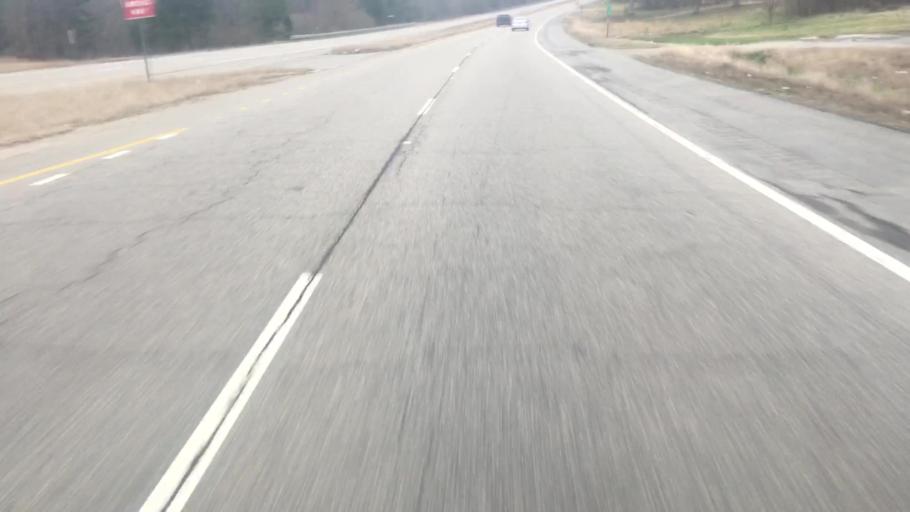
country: US
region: Alabama
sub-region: Walker County
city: Cordova
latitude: 33.8191
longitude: -87.1523
